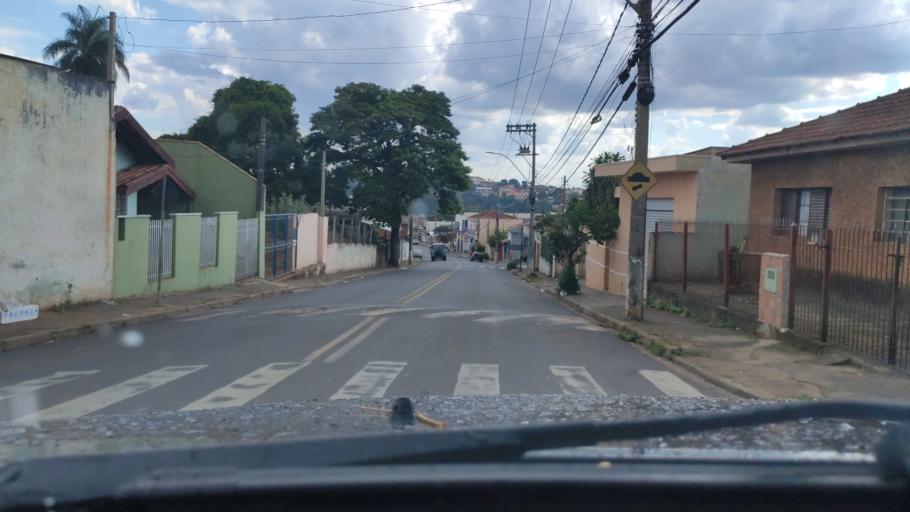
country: BR
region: Sao Paulo
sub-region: Itapira
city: Itapira
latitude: -22.4380
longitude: -46.8109
